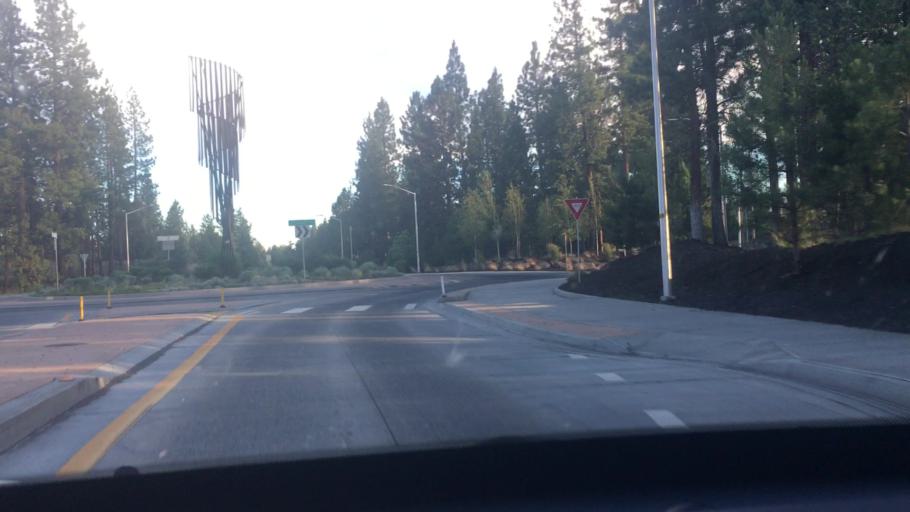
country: US
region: Oregon
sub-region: Deschutes County
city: Bend
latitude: 44.0478
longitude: -121.3441
